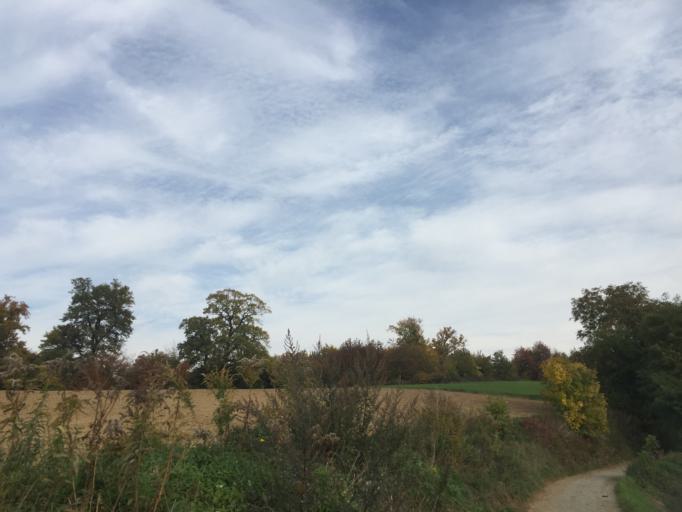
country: DE
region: Hesse
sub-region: Regierungsbezirk Darmstadt
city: Bensheim
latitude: 49.6887
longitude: 8.6552
